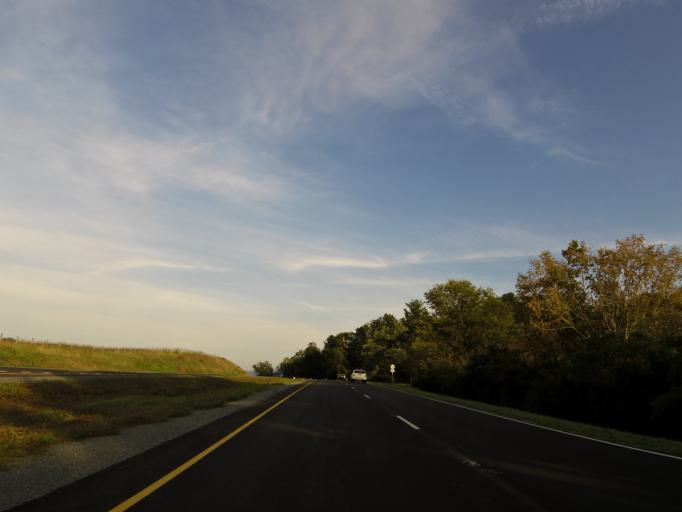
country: US
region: Virginia
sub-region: Washington County
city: Abingdon
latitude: 36.6826
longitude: -81.8815
